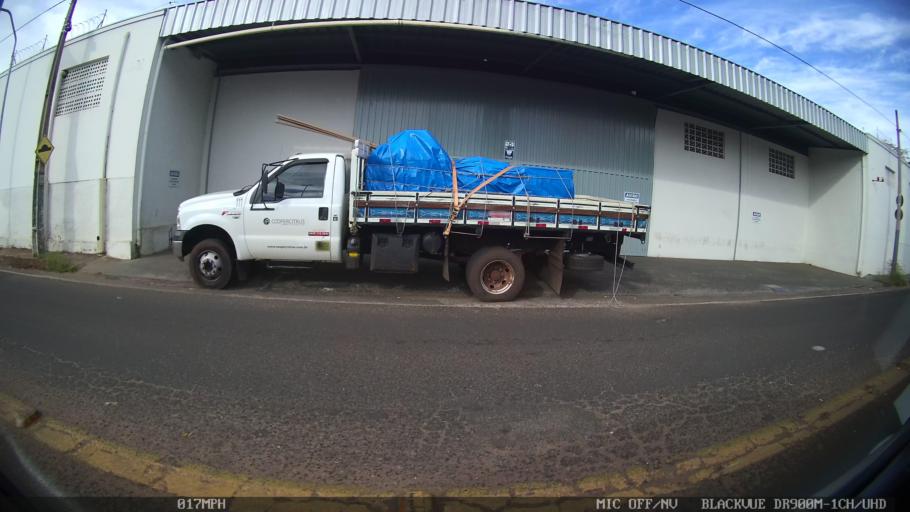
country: BR
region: Sao Paulo
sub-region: Catanduva
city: Catanduva
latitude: -21.1287
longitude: -48.9805
